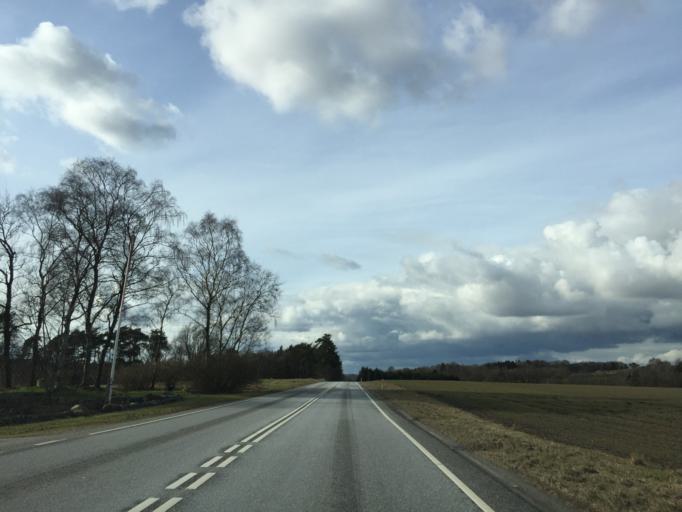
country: DK
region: Central Jutland
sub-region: Favrskov Kommune
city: Hammel
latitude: 56.2109
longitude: 9.7797
